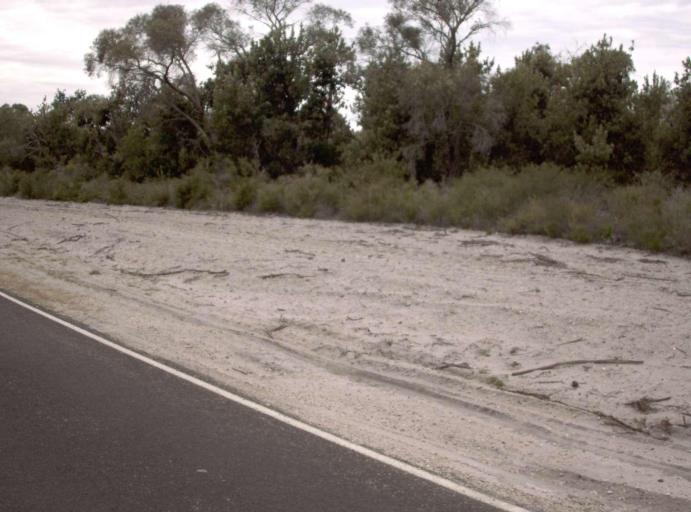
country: AU
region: Victoria
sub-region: Wellington
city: Sale
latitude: -38.1710
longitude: 147.3843
